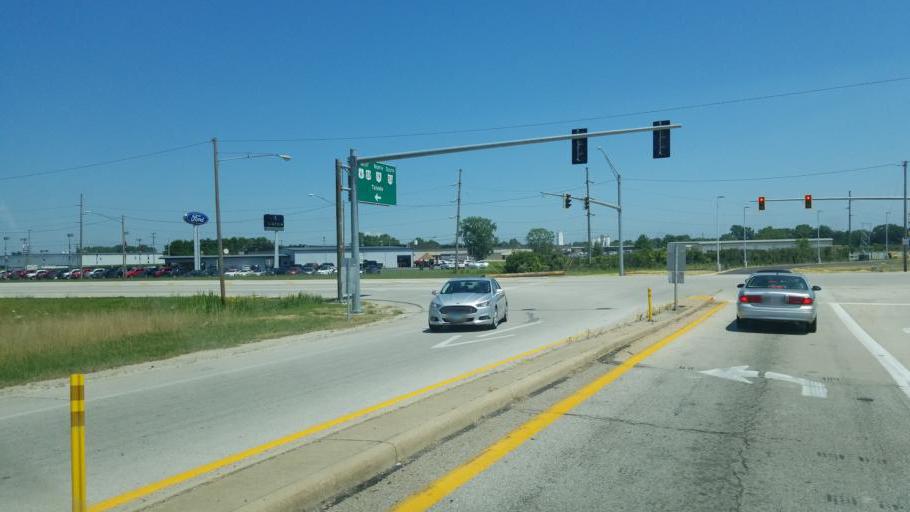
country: US
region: Ohio
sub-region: Sandusky County
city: Fremont
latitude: 41.3709
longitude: -83.1177
